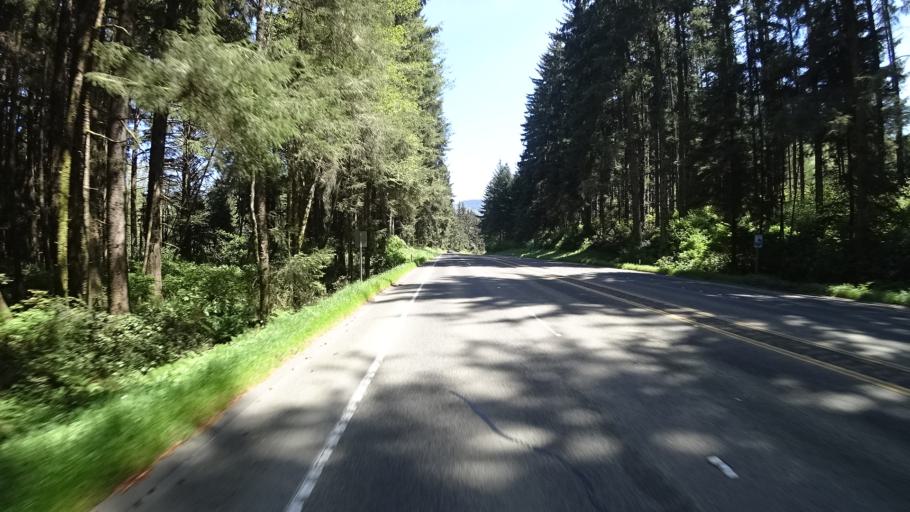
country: US
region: California
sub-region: Humboldt County
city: Westhaven-Moonstone
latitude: 41.1579
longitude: -124.1238
